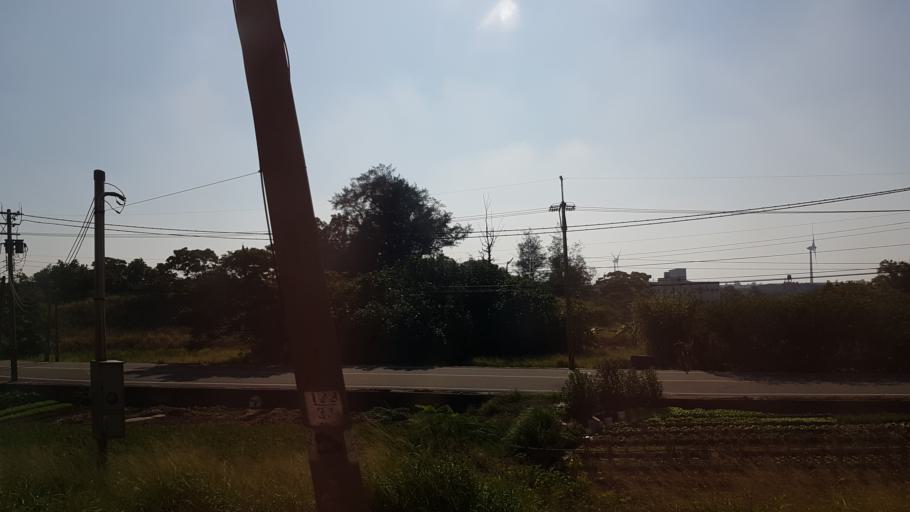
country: TW
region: Taiwan
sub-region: Hsinchu
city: Hsinchu
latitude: 24.7074
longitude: 120.8710
